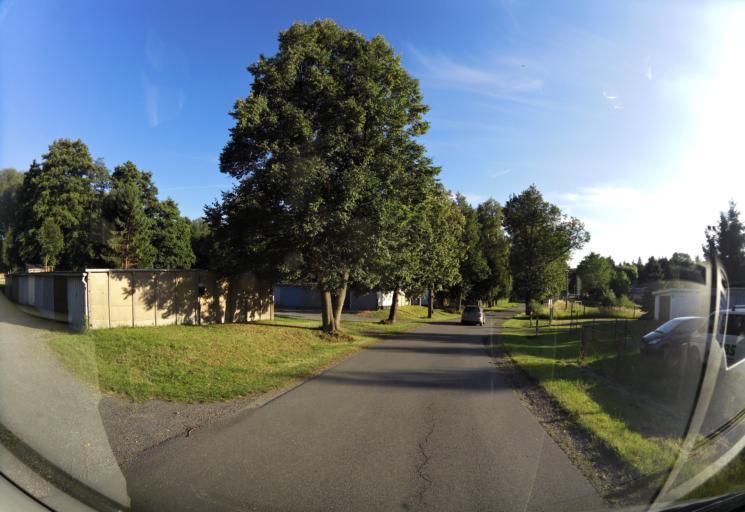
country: DE
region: Thuringia
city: Schleiz
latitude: 50.5735
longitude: 11.8161
